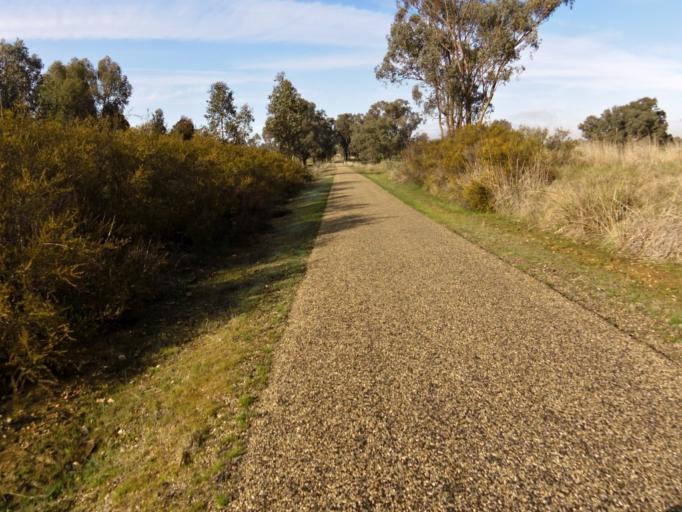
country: AU
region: Victoria
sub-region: Wangaratta
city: Wangaratta
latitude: -36.4200
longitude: 146.5502
